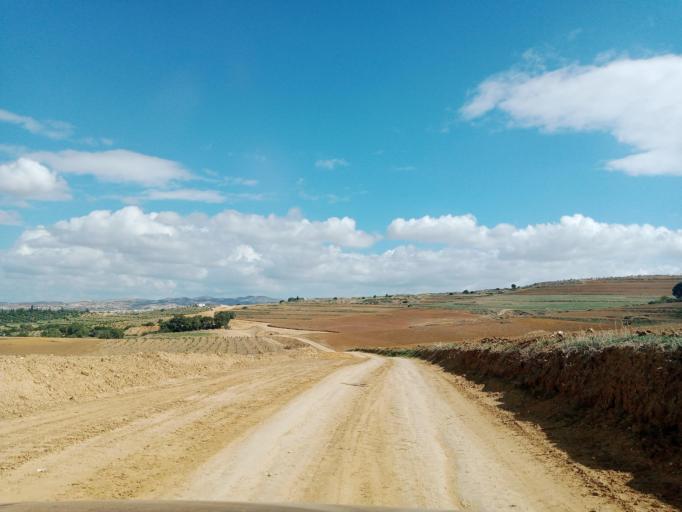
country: TN
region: Tunis
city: Oued Lill
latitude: 36.8121
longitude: 9.9950
